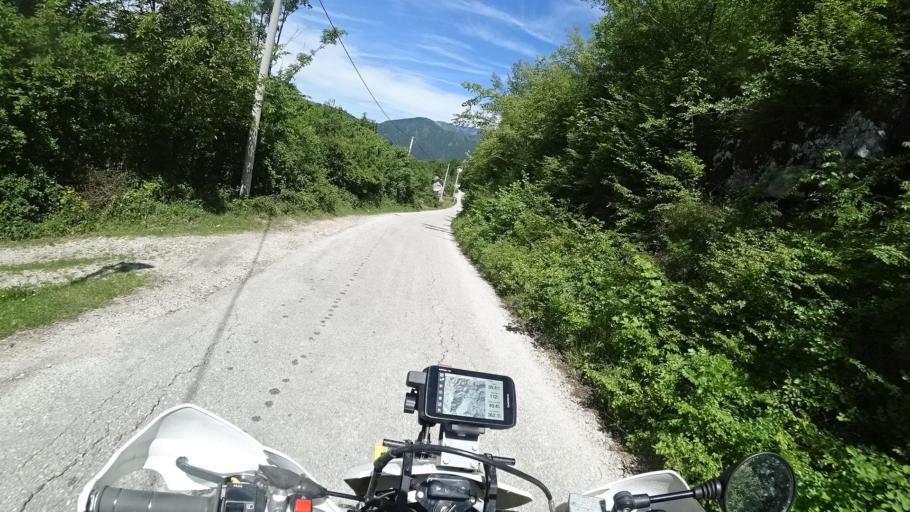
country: BA
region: Federation of Bosnia and Herzegovina
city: Bijela
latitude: 43.6123
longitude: 17.9561
